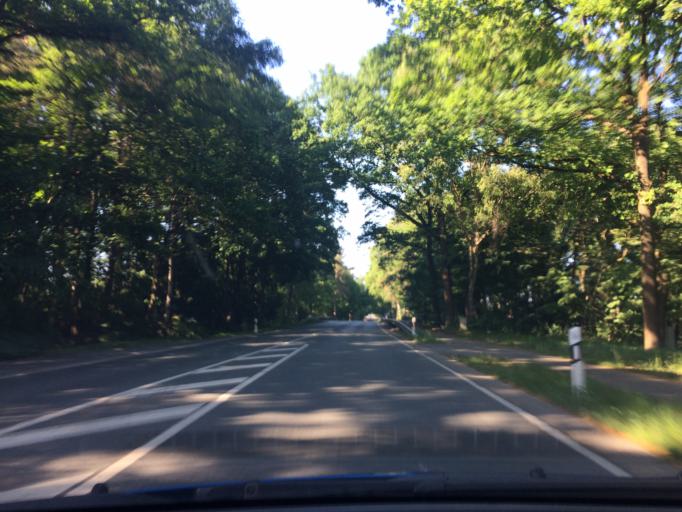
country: DE
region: Lower Saxony
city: Soltau
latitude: 53.0197
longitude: 9.8483
